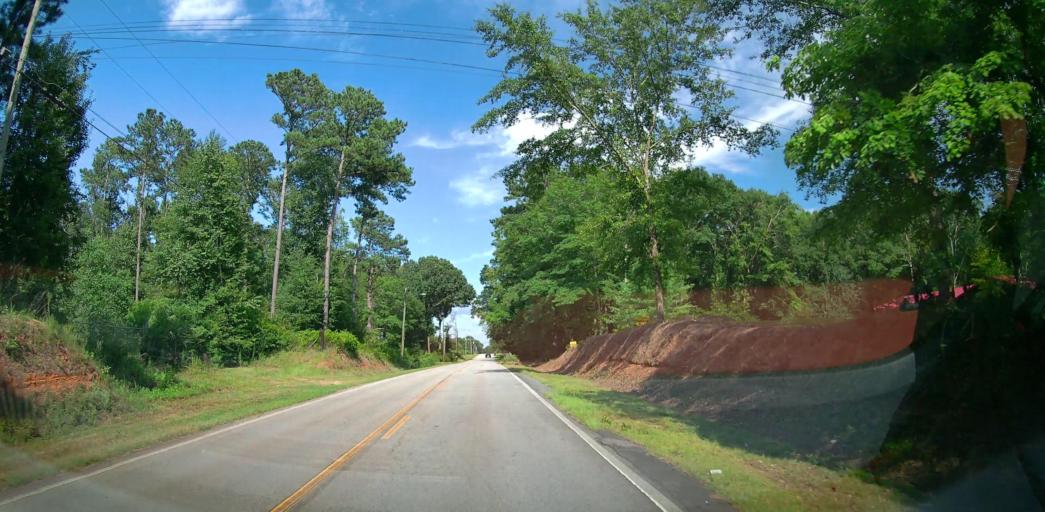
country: US
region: Georgia
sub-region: Houston County
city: Warner Robins
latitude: 32.5382
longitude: -83.6518
